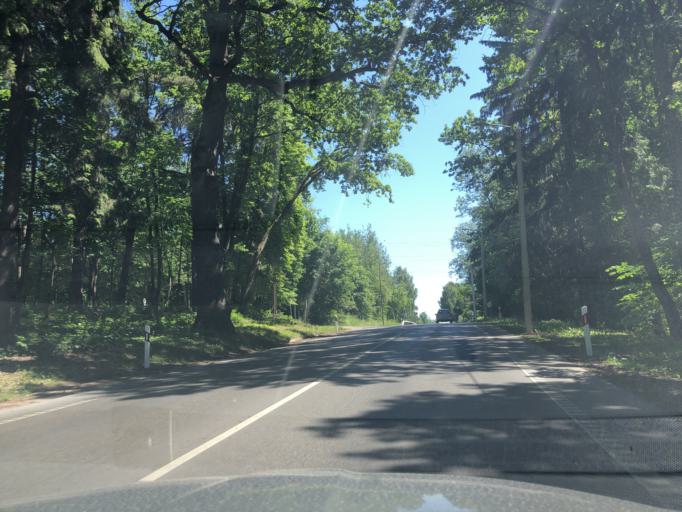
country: LT
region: Kauno apskritis
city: Dainava (Kaunas)
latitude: 54.8717
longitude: 23.9874
